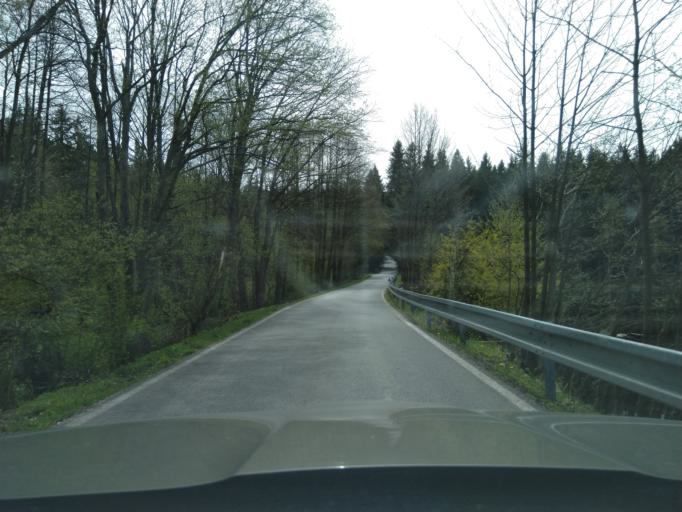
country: CZ
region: Jihocesky
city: Vacov
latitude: 49.1618
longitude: 13.6885
